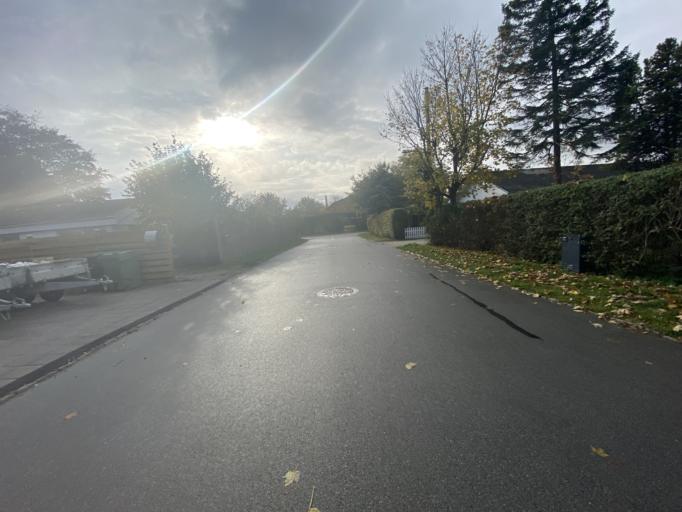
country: DK
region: Capital Region
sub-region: Dragor Kommune
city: Dragor
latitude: 55.5844
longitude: 12.6462
